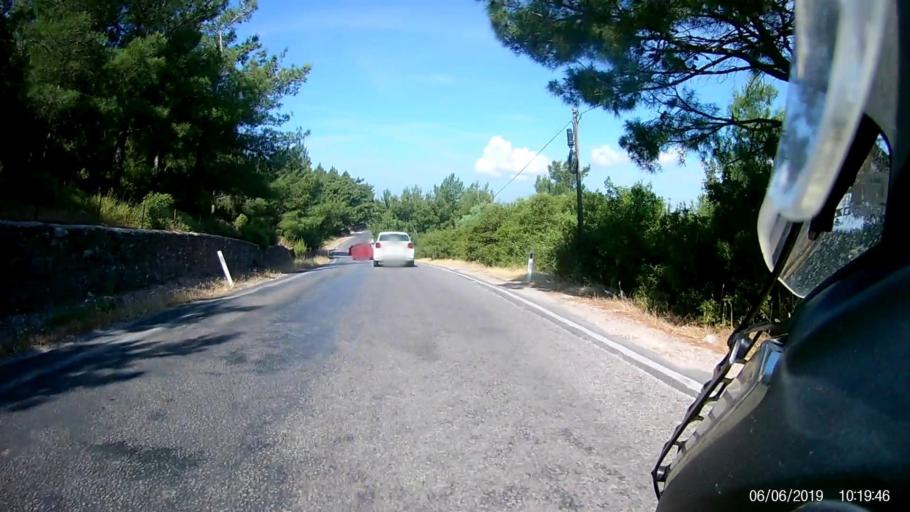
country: TR
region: Canakkale
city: Ayvacik
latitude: 39.5215
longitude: 26.4587
